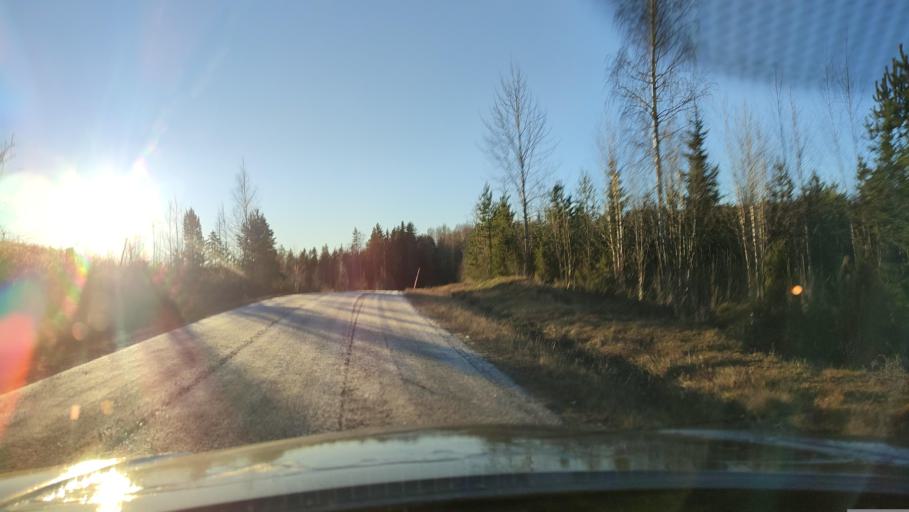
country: SE
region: Vaesterbotten
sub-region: Skelleftea Kommun
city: Viken
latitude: 64.7188
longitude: 20.9158
